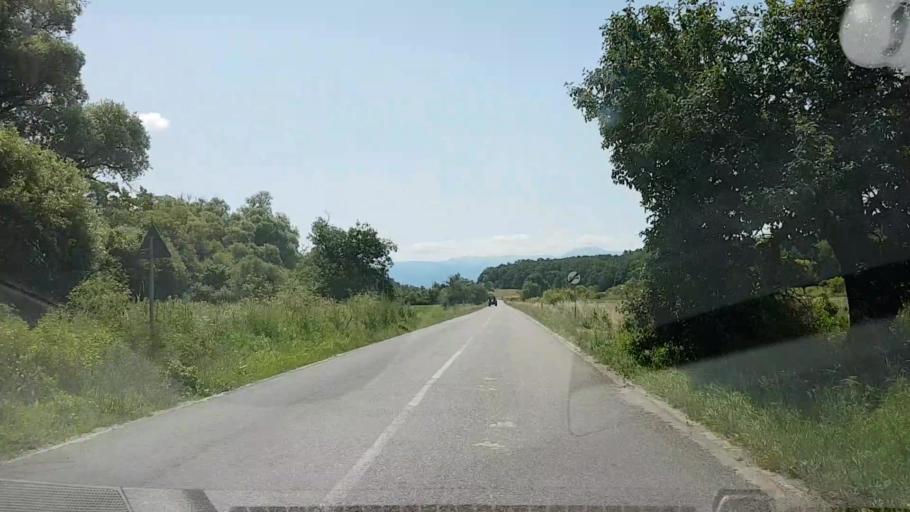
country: RO
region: Brasov
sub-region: Comuna Cincu
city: Cincu
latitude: 45.8766
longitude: 24.8184
